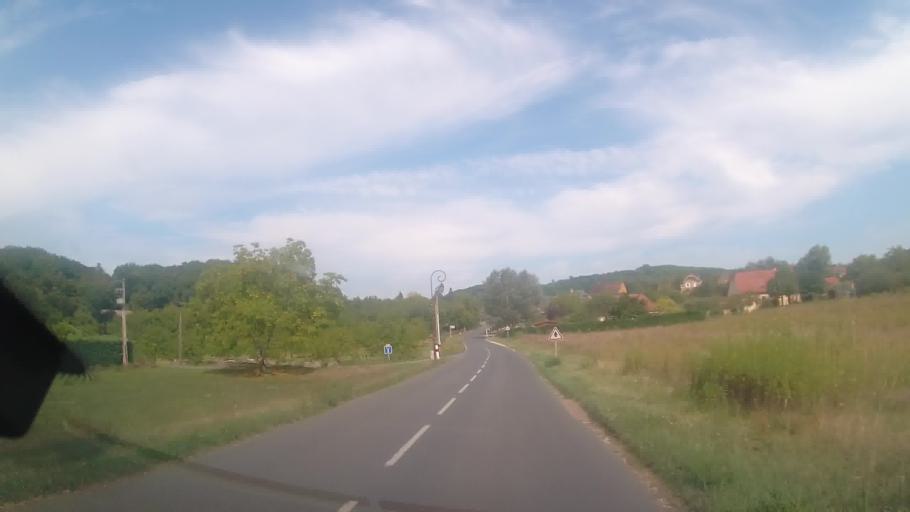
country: FR
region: Aquitaine
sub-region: Departement de la Dordogne
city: Carsac-Aillac
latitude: 44.8288
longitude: 1.3063
